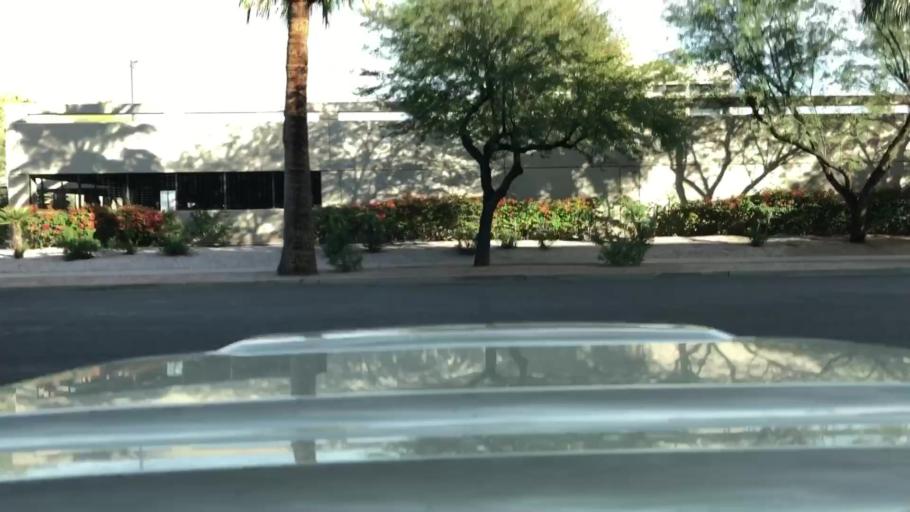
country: US
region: Arizona
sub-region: Maricopa County
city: Phoenix
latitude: 33.4490
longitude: -112.0857
